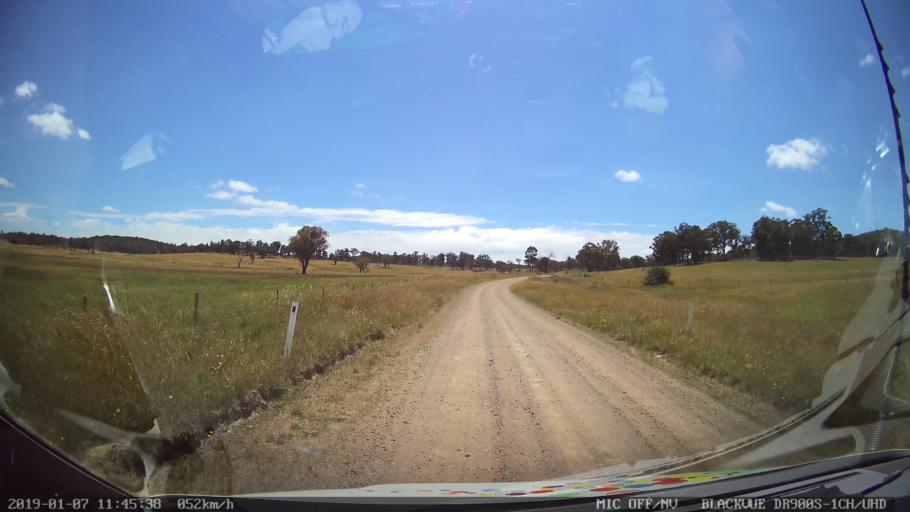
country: AU
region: New South Wales
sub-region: Guyra
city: Guyra
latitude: -30.3453
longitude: 151.6070
